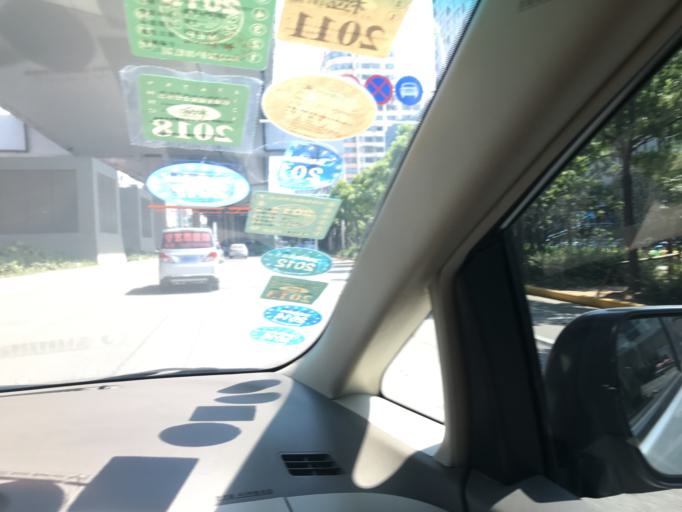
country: CN
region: Hubei
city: Shilipu
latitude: 30.5651
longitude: 114.2054
